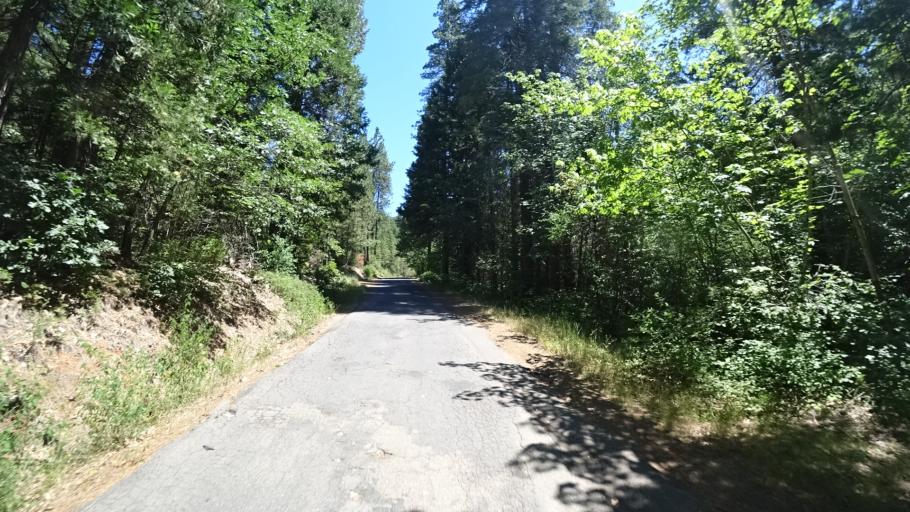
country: US
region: California
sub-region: Calaveras County
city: Arnold
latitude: 38.2195
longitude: -120.3408
